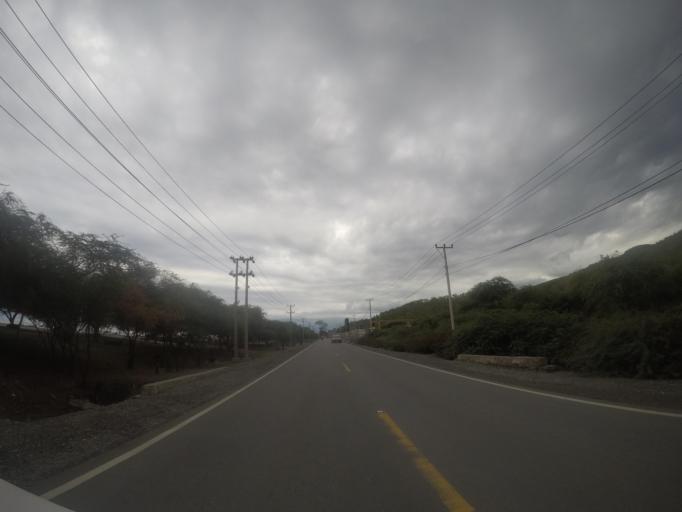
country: TL
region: Liquica
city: Liquica
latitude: -8.5648
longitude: 125.3983
